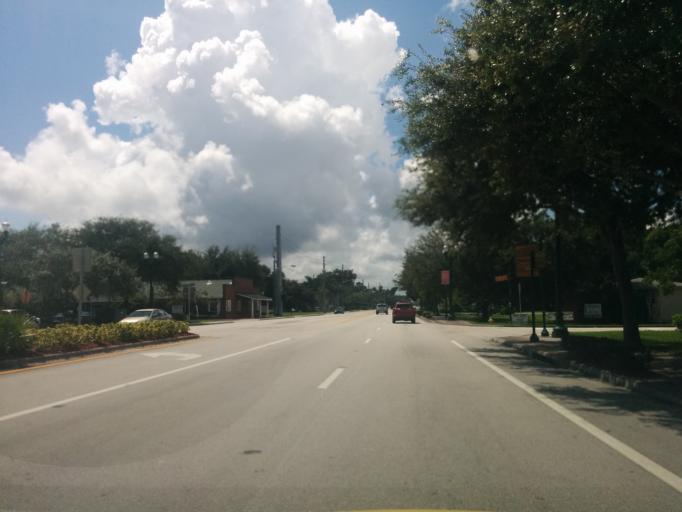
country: US
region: Florida
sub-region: Broward County
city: Davie
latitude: 26.0633
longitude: -80.2322
